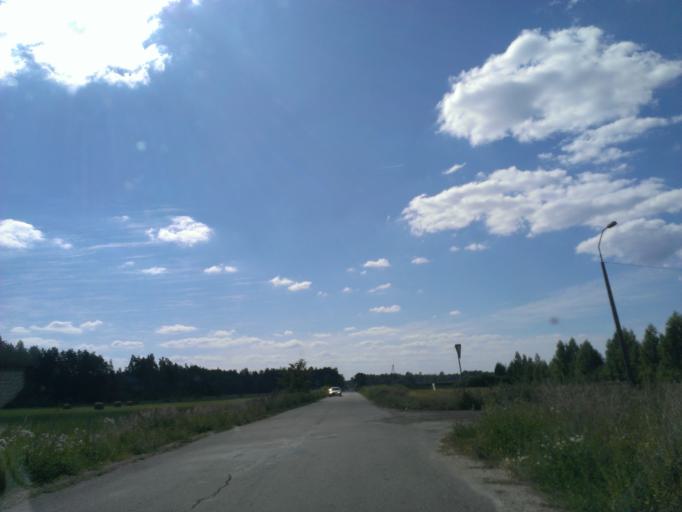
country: LV
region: Adazi
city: Adazi
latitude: 57.0817
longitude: 24.2917
